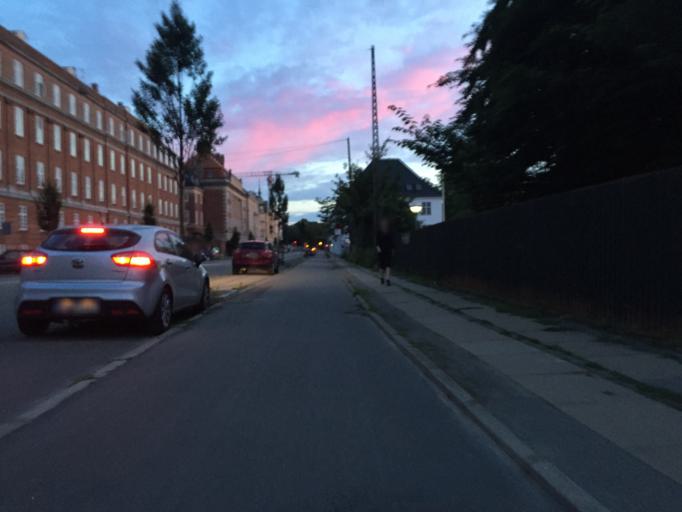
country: DK
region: Capital Region
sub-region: Kobenhavn
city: Christianshavn
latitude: 55.6956
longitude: 12.5885
